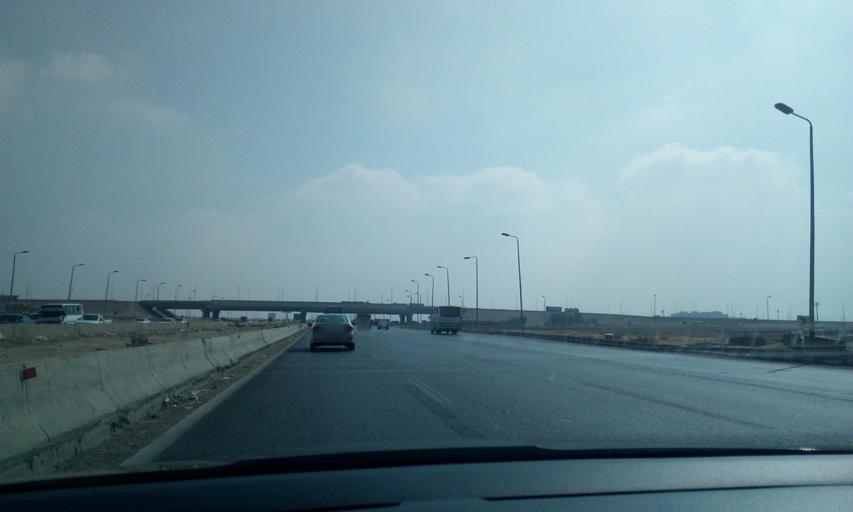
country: EG
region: Eastern Province
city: Bilbays
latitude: 30.2220
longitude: 31.6928
